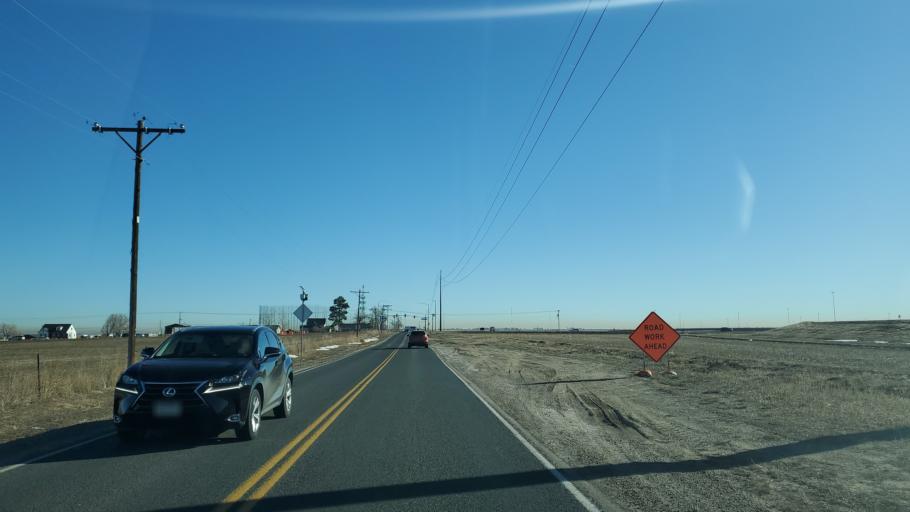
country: US
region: Colorado
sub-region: Boulder County
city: Erie
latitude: 39.9868
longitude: -105.0007
